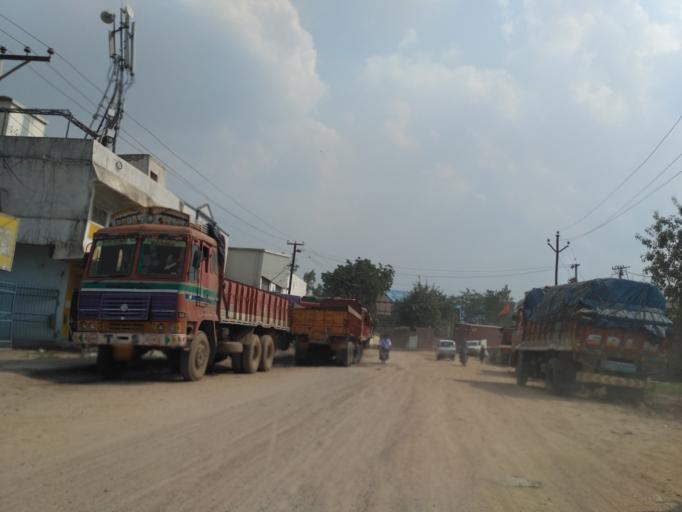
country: IN
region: Telangana
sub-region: Rangareddi
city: Kukatpalli
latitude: 17.4651
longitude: 78.4210
